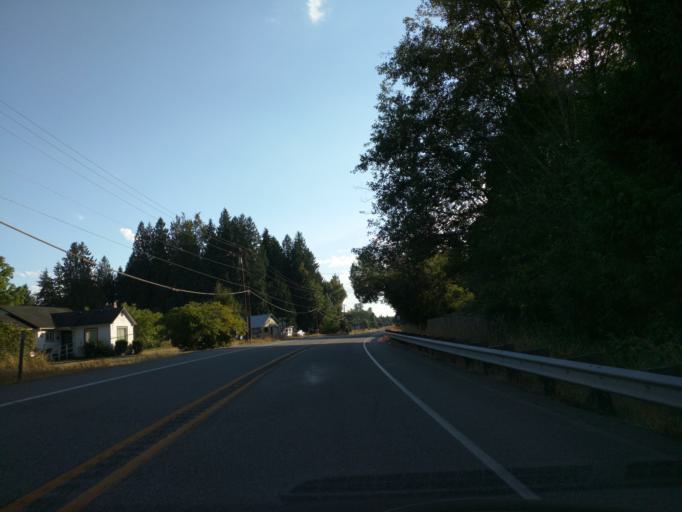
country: US
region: Washington
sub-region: Snohomish County
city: Arlington Heights
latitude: 48.2361
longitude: -122.0622
